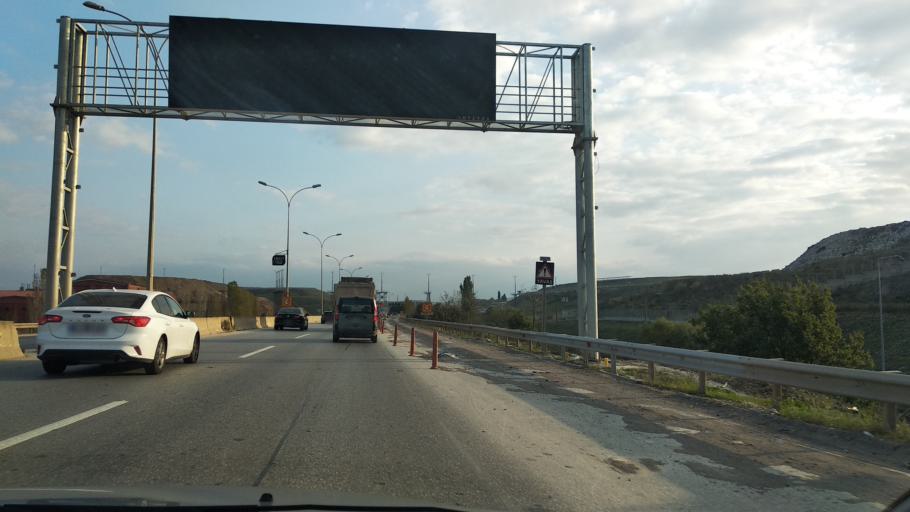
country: TR
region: Istanbul
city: Pendik
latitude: 40.9091
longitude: 29.3269
